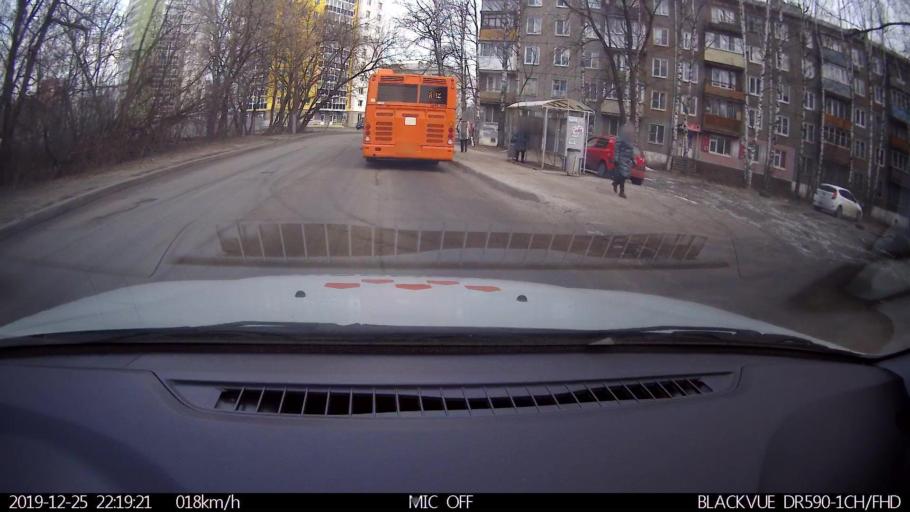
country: RU
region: Nizjnij Novgorod
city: Gorbatovka
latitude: 56.3383
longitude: 43.8429
